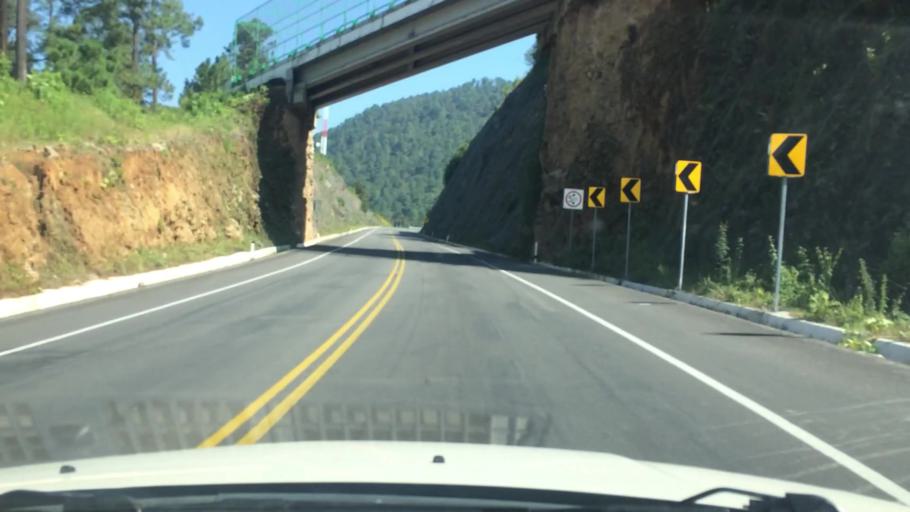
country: MX
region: Mexico
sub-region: Amanalco
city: Polvillos (San Bartolo Quinta Seccion)
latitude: 19.2300
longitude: -100.0732
